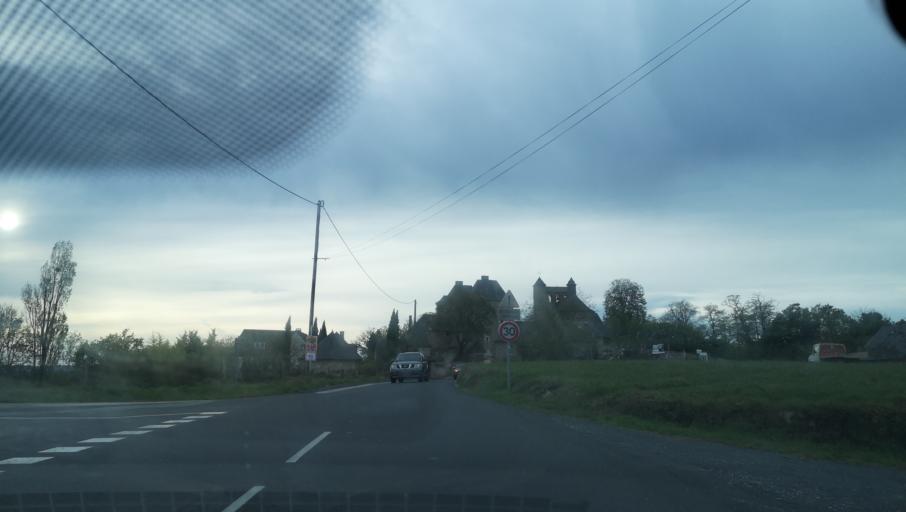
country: FR
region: Limousin
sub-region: Departement de la Correze
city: Brive-la-Gaillarde
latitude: 45.1035
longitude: 1.5283
